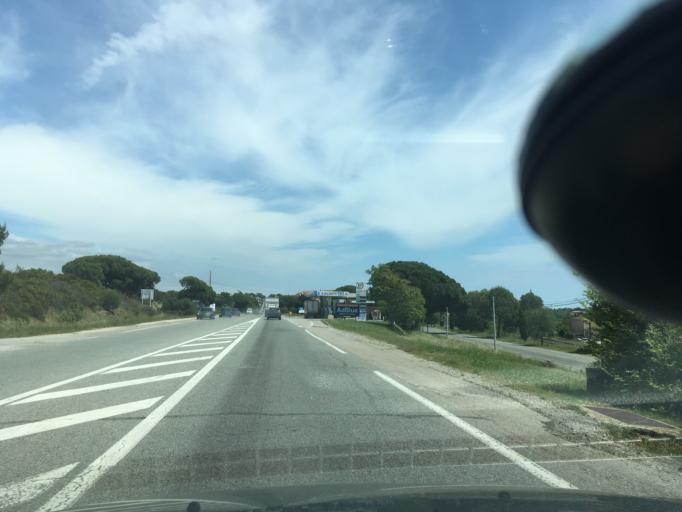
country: FR
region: Provence-Alpes-Cote d'Azur
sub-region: Departement du Var
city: Puget-sur-Argens
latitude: 43.4589
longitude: 6.6697
